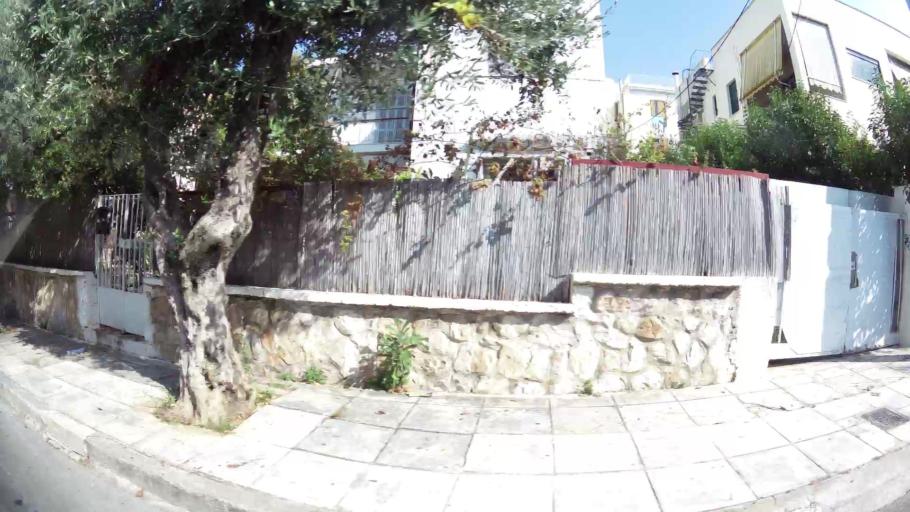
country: GR
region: Attica
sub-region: Nomarchia Athinas
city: Cholargos
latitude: 38.0006
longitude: 23.7984
